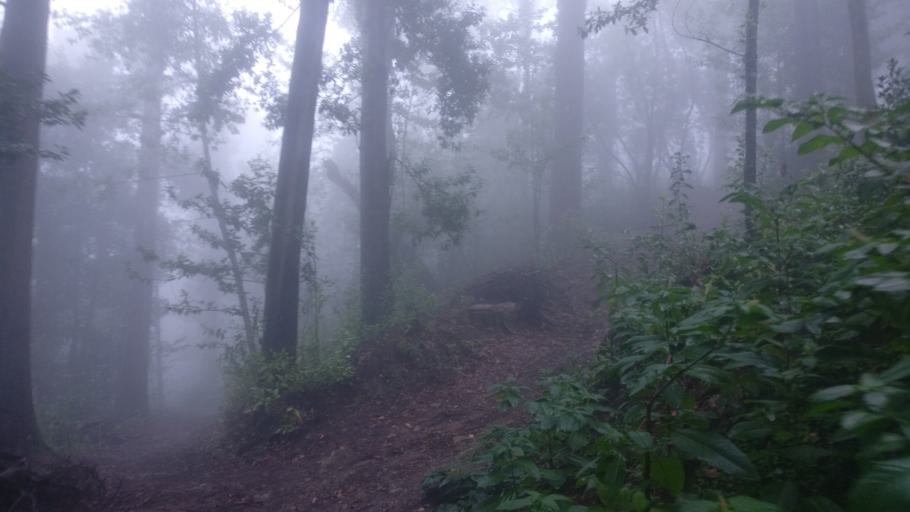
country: PT
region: Aveiro
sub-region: Mealhada
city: Pampilhosa do Botao
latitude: 40.3768
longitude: -8.3674
